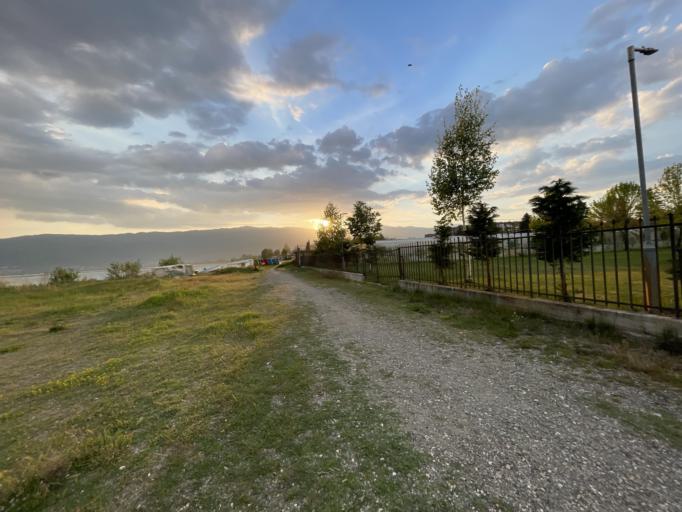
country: MK
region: Struga
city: Struga
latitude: 41.1722
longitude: 20.6856
